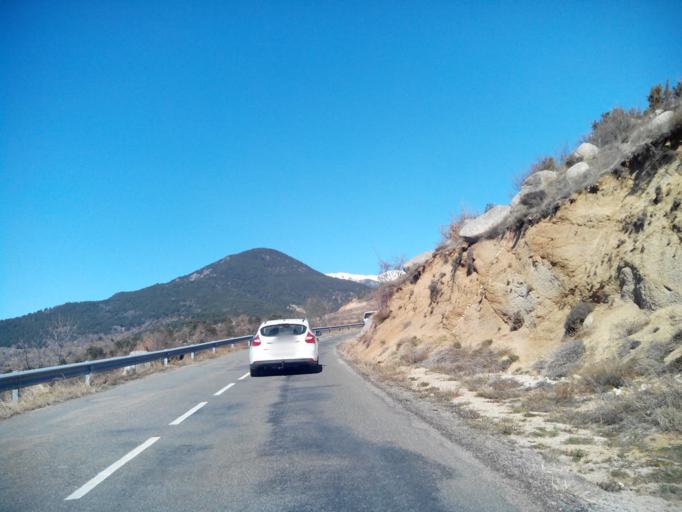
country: ES
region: Catalonia
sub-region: Provincia de Lleida
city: Lles de Cerdanya
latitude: 42.3810
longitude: 1.6856
